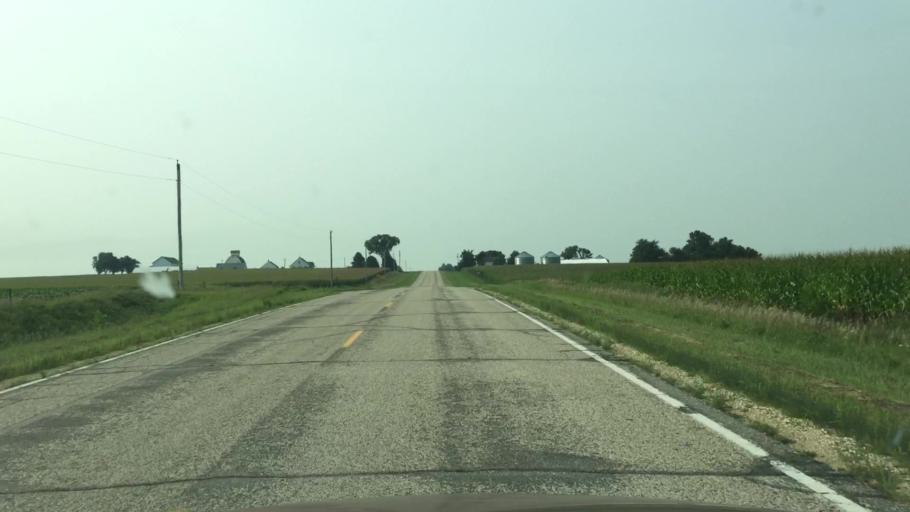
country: US
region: Iowa
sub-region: O'Brien County
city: Sheldon
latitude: 43.2738
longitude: -95.7829
